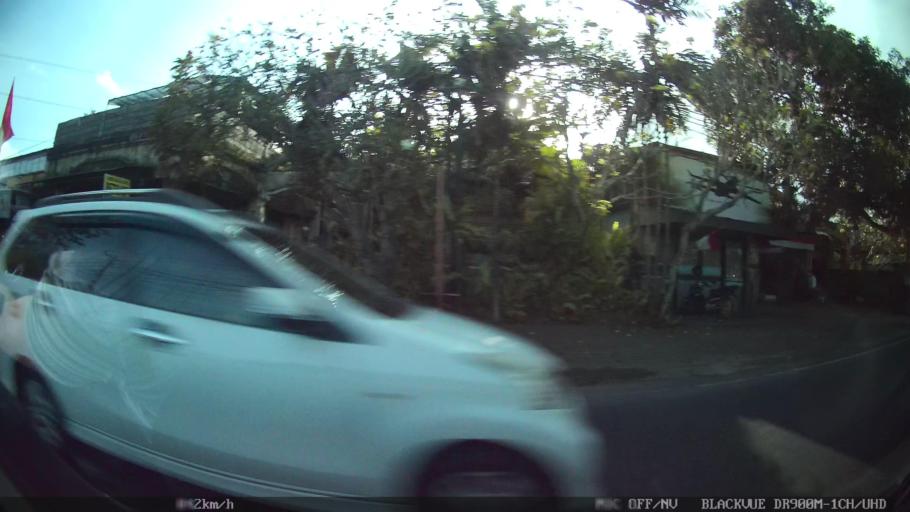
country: ID
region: Bali
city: Banjar Batur
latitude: -8.5912
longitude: 115.2154
